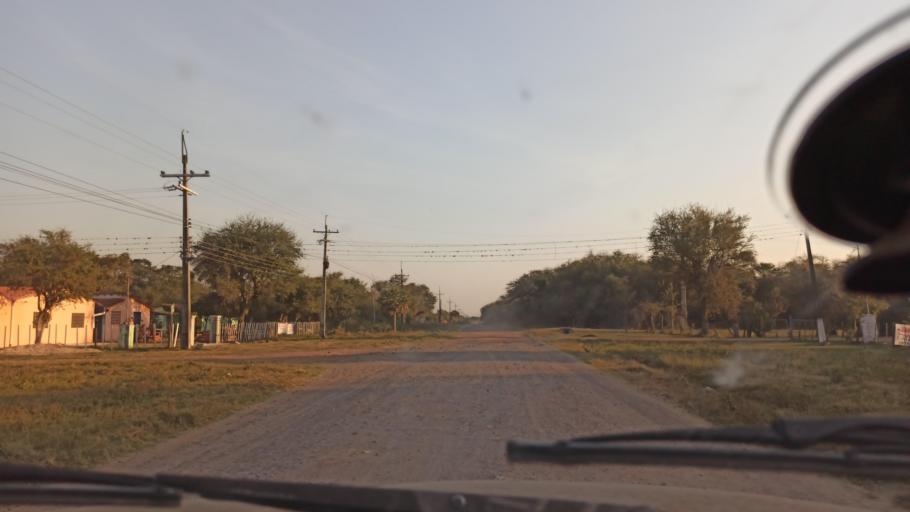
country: PY
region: Presidente Hayes
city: Nanawa
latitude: -25.2352
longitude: -57.6322
